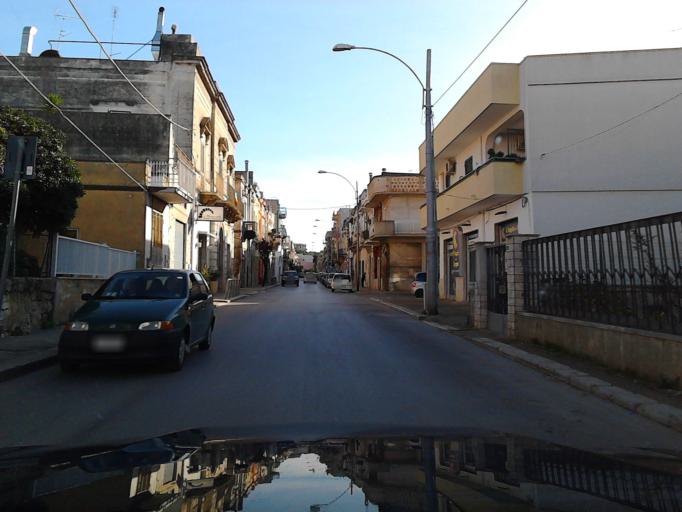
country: IT
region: Apulia
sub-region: Provincia di Bari
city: Rutigliano
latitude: 41.0152
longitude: 17.0009
